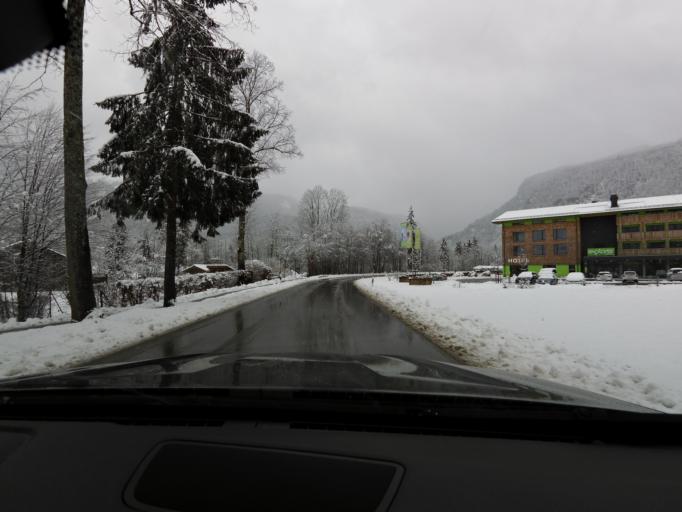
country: DE
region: Bavaria
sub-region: Upper Bavaria
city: Schoenau am Koenigssee
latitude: 47.5989
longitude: 12.9852
